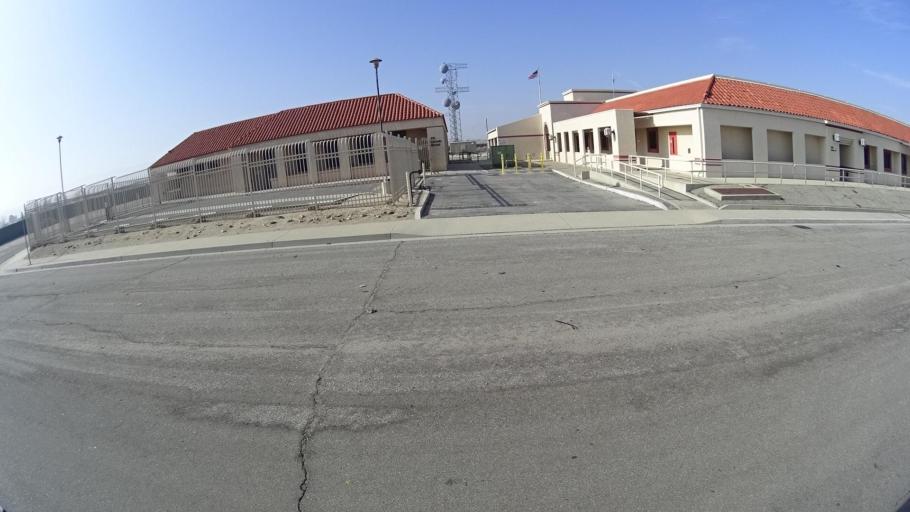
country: US
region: California
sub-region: Kern County
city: Ford City
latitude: 35.1556
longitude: -119.4652
